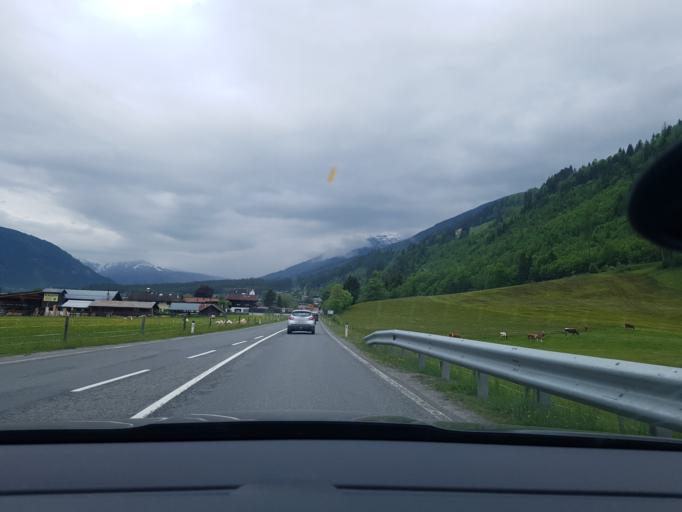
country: AT
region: Salzburg
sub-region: Politischer Bezirk Zell am See
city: Neukirchen am Grossvenediger
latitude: 47.2546
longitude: 12.2888
